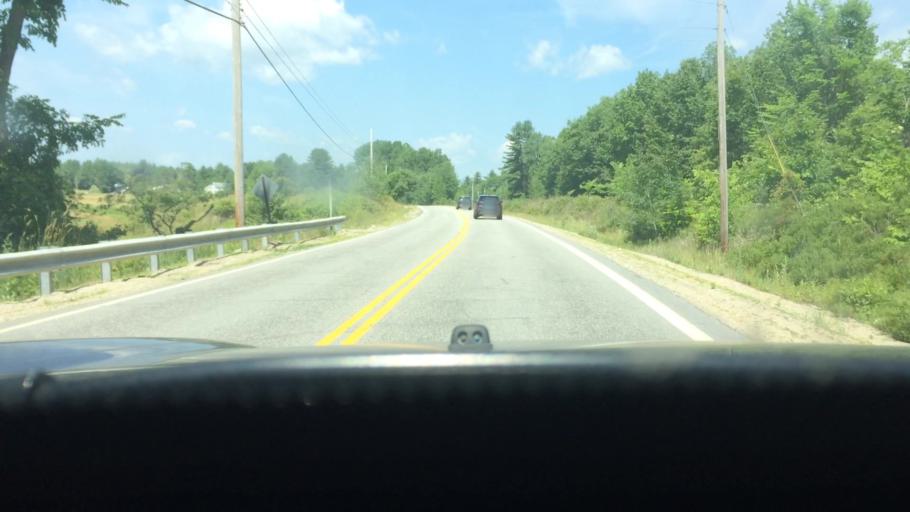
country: US
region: Maine
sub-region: Androscoggin County
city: Mechanic Falls
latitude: 44.1303
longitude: -70.4380
